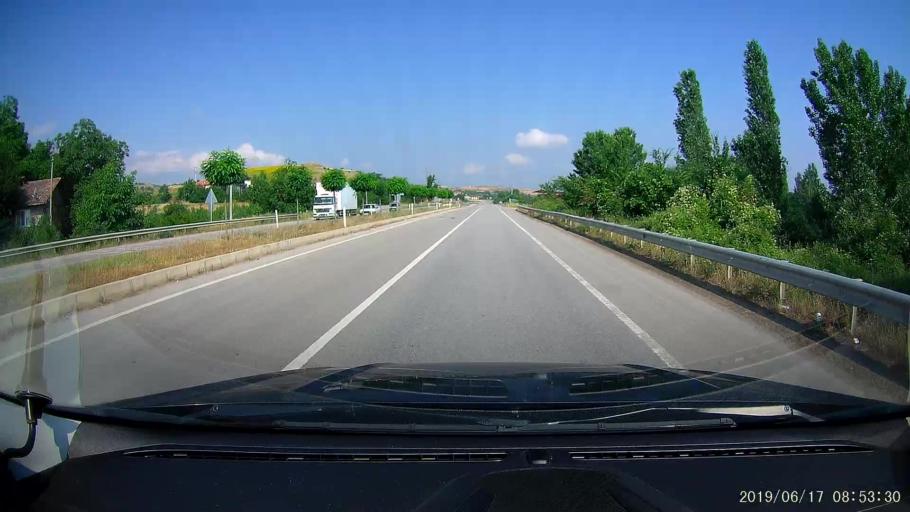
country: TR
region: Tokat
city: Erbaa
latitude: 40.7103
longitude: 36.4805
